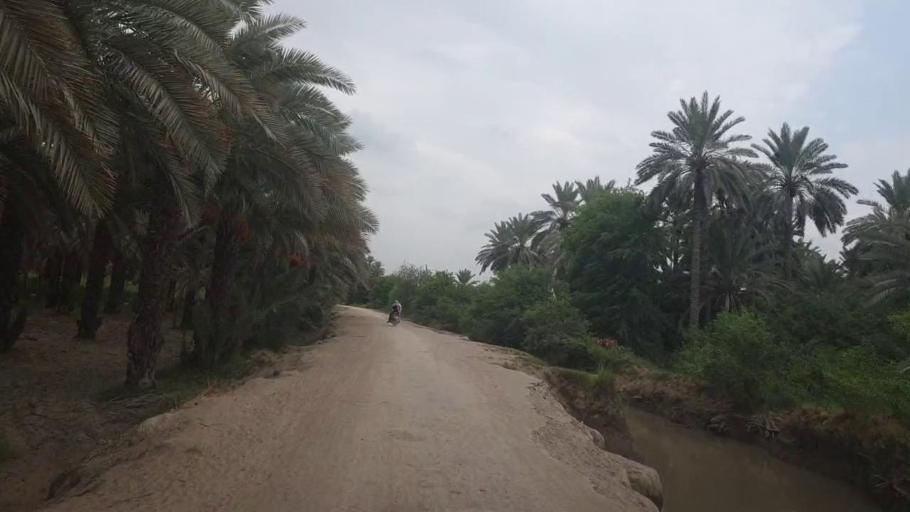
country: PK
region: Sindh
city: Khairpur
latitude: 27.5831
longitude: 68.7122
